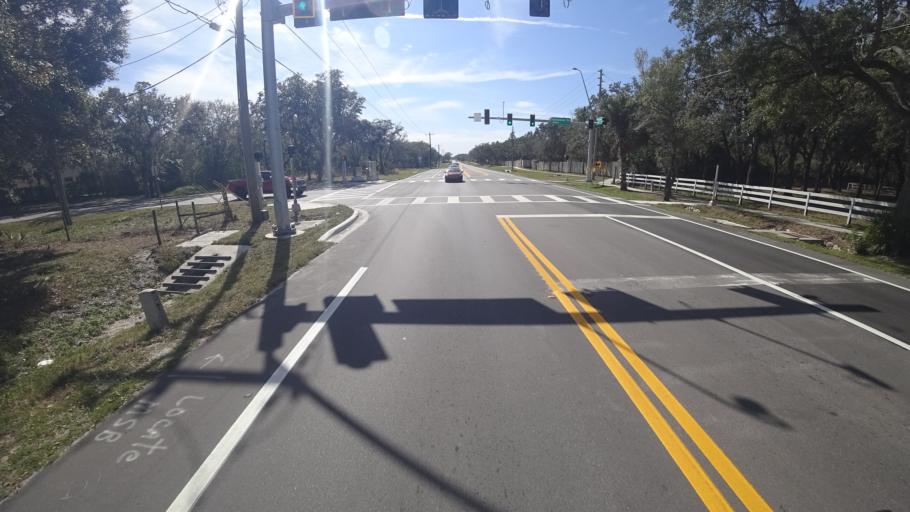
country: US
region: Florida
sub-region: Manatee County
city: Ellenton
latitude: 27.5356
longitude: -82.4257
